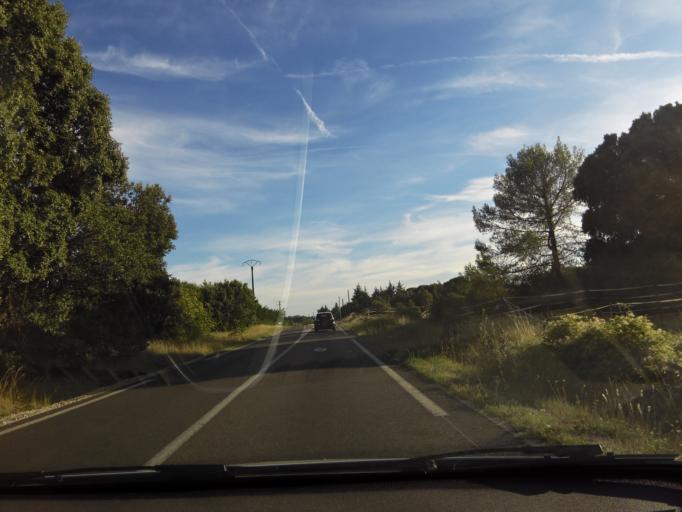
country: FR
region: Languedoc-Roussillon
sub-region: Departement de l'Herault
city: Saint-Mathieu-de-Treviers
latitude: 43.8112
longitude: 3.8881
